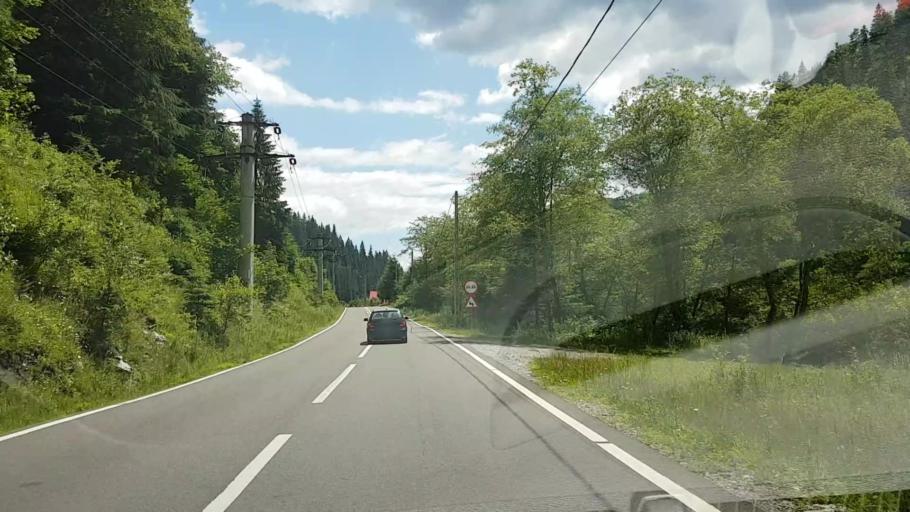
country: RO
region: Suceava
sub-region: Comuna Brosteni
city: Brosteni
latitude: 47.2716
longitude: 25.6497
